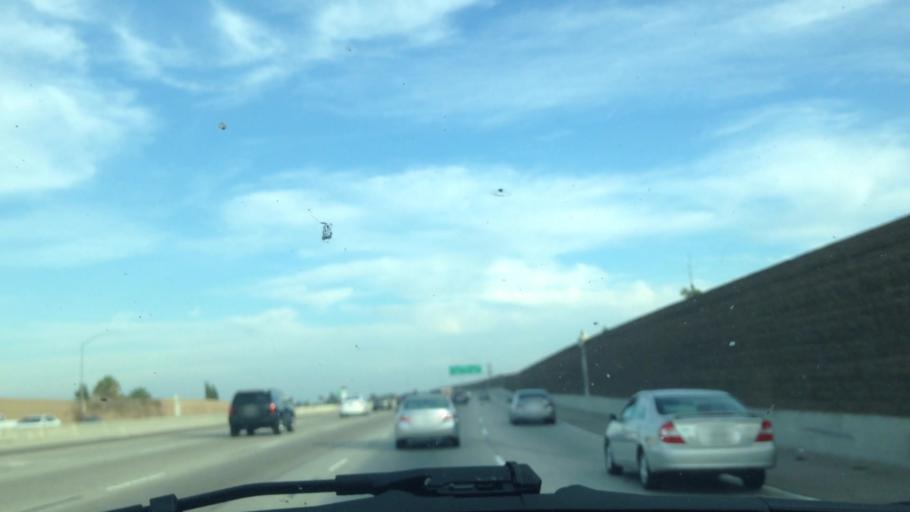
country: US
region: California
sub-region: Orange County
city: Midway City
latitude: 33.7689
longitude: -117.9788
